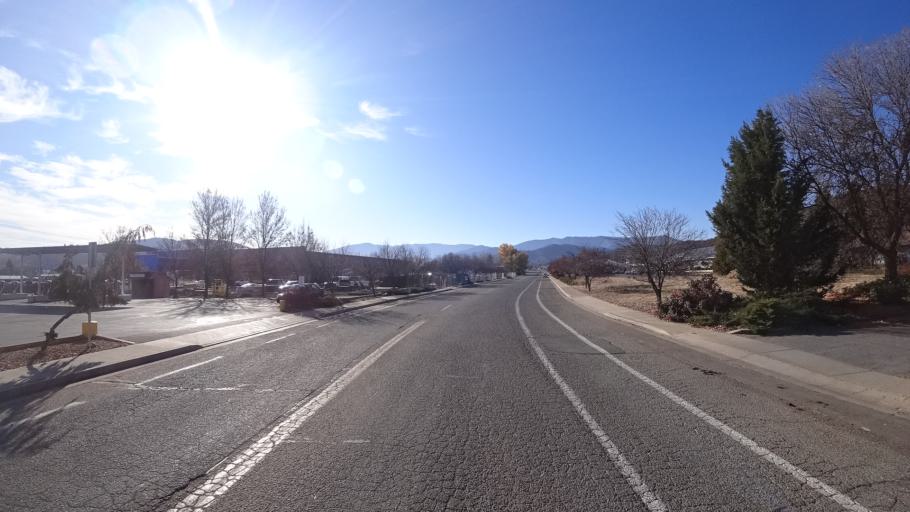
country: US
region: California
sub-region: Siskiyou County
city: Yreka
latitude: 41.7117
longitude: -122.6441
